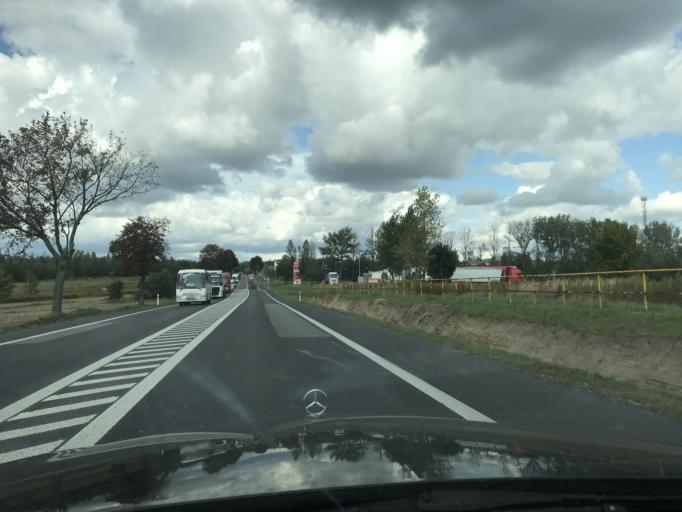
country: PL
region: Lublin Voivodeship
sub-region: Powiat lubelski
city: Niemce
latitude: 51.3688
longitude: 22.6322
